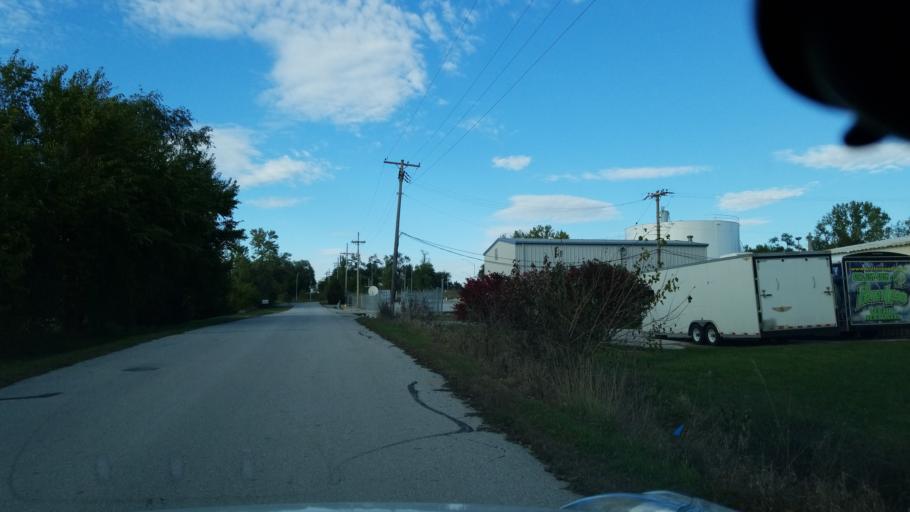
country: US
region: Nebraska
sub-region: Sarpy County
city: Offutt Air Force Base
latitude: 41.1152
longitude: -95.9328
